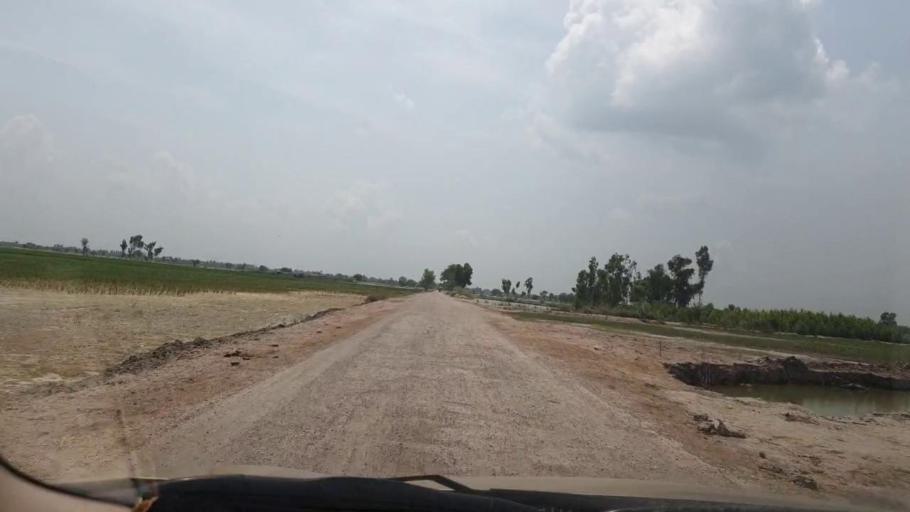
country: PK
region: Sindh
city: Larkana
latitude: 27.6179
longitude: 68.1418
